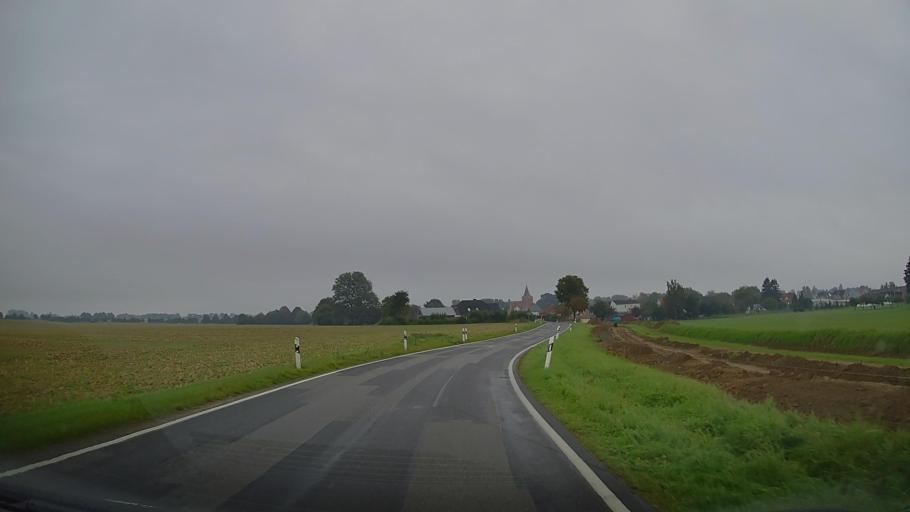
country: DE
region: Mecklenburg-Vorpommern
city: Kalkhorst
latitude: 53.9738
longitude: 11.0369
